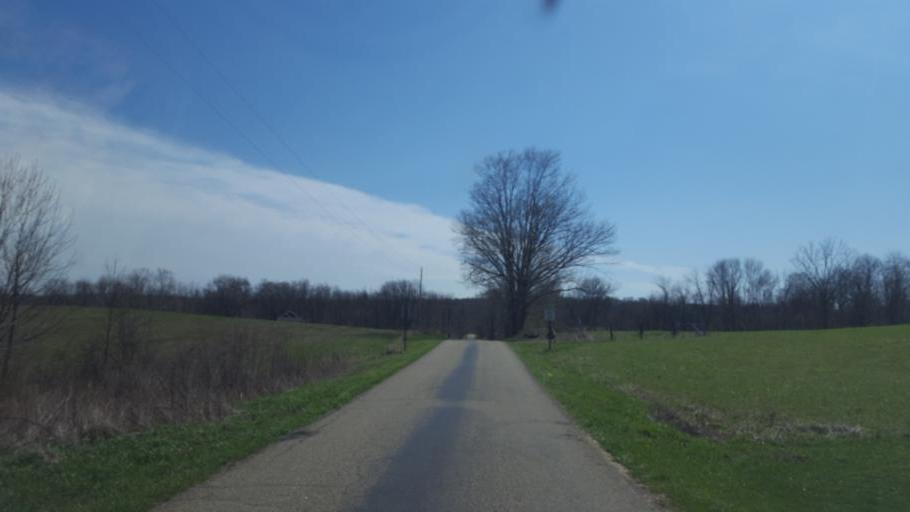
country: US
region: Ohio
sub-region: Knox County
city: Gambier
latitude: 40.3559
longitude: -82.3935
